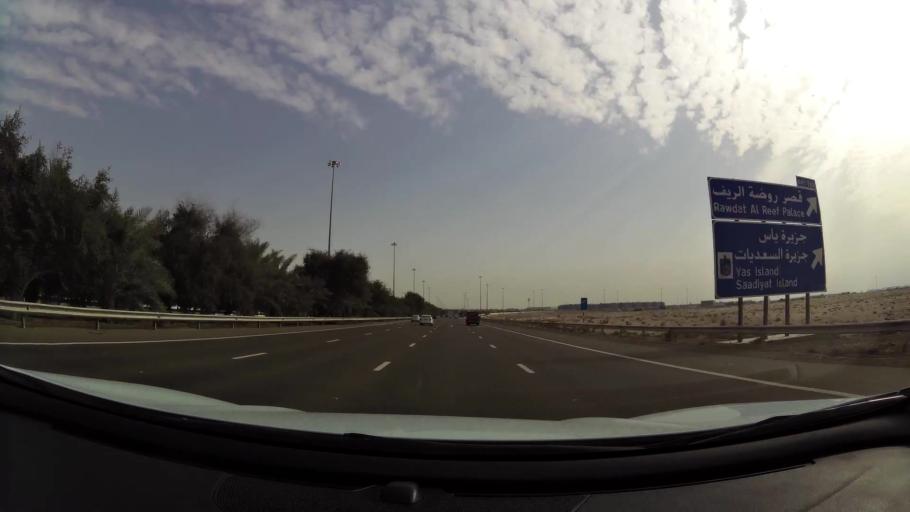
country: AE
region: Abu Dhabi
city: Abu Dhabi
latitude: 24.4696
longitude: 54.6764
